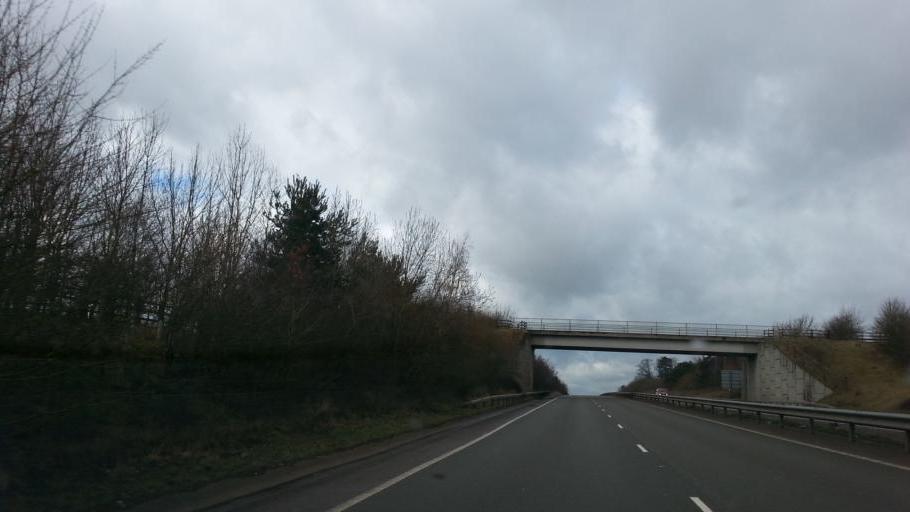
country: GB
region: England
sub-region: Leicestershire
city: Great Glen
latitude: 52.5594
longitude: -1.0170
